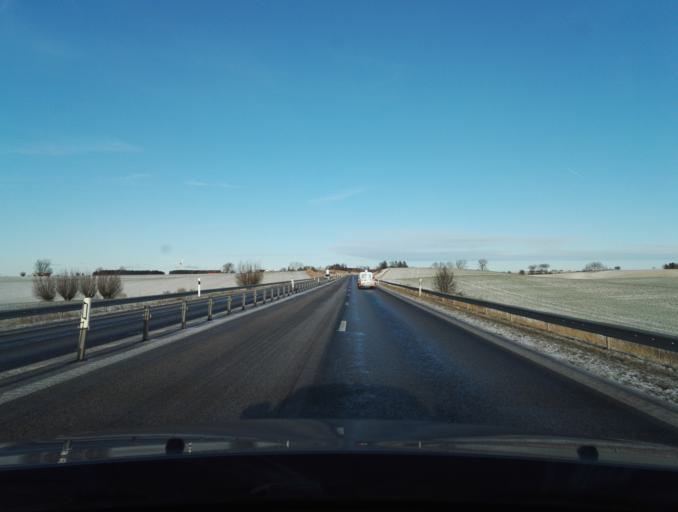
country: SE
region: Skane
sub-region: Svedala Kommun
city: Svedala
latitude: 55.4594
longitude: 13.1921
